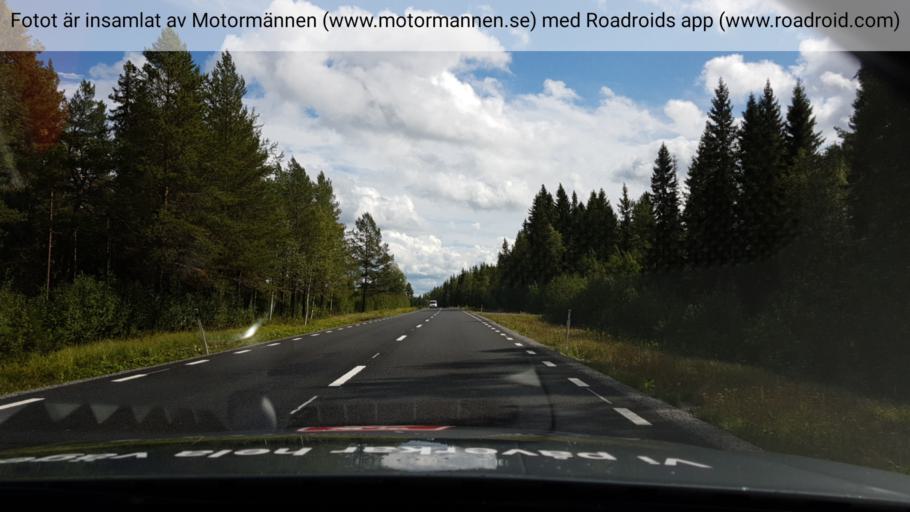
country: SE
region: Jaemtland
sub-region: OEstersunds Kommun
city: Brunflo
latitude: 63.1998
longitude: 14.9479
